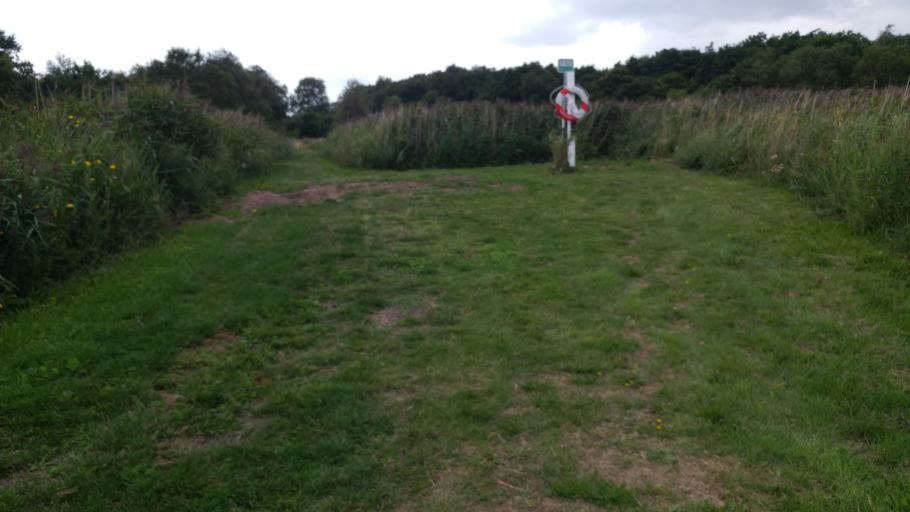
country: DK
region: Central Jutland
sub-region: Norddjurs Kommune
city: Allingabro
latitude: 56.5501
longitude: 10.3751
